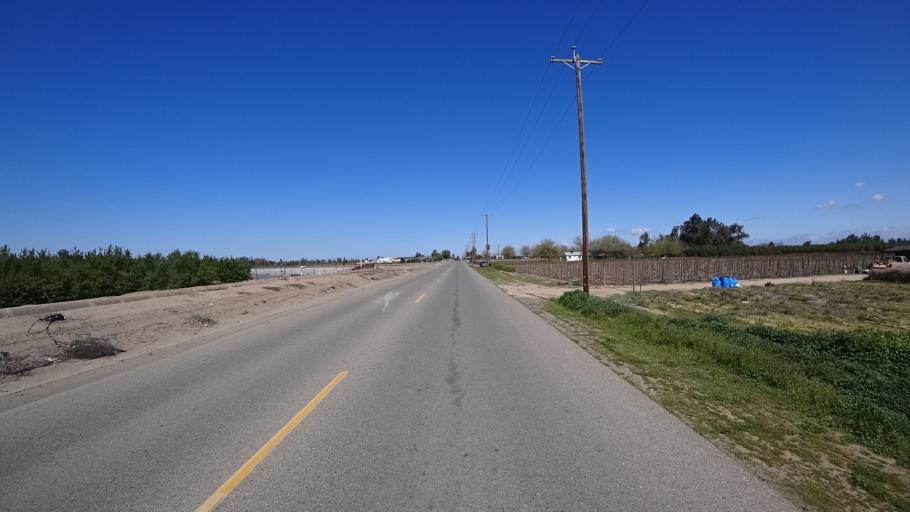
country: US
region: California
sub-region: Fresno County
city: West Park
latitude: 36.7091
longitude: -119.8445
